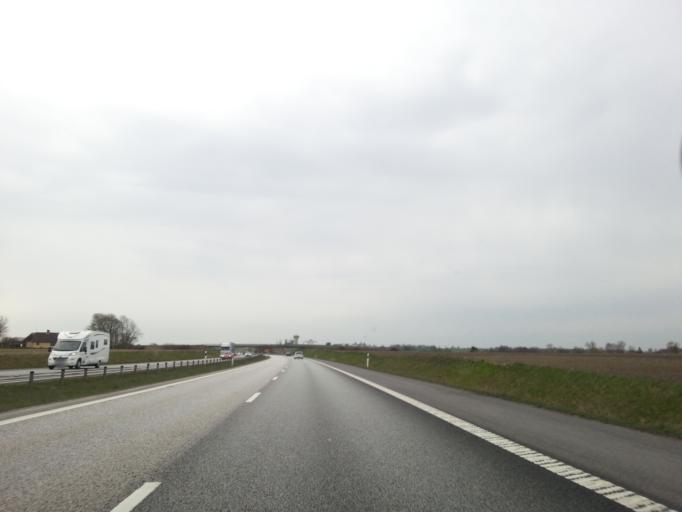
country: SE
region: Skane
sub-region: Angelholms Kommun
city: AEngelholm
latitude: 56.2743
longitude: 12.8950
